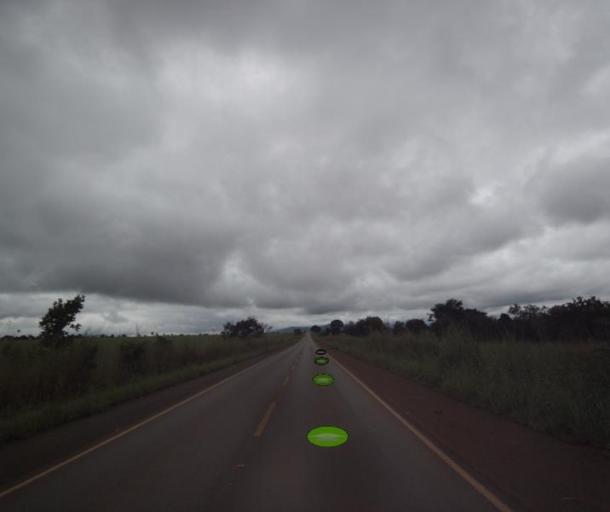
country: BR
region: Goias
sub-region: Barro Alto
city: Barro Alto
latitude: -14.8432
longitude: -49.0288
